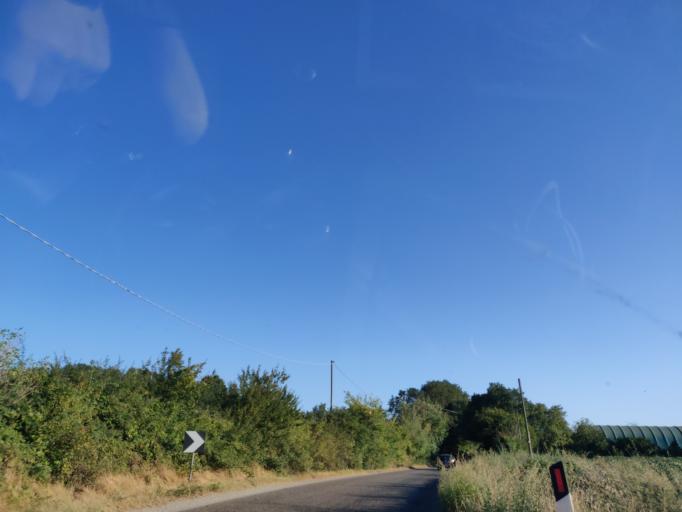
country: IT
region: Latium
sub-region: Provincia di Viterbo
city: Grotte di Castro
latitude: 42.6856
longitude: 11.8753
